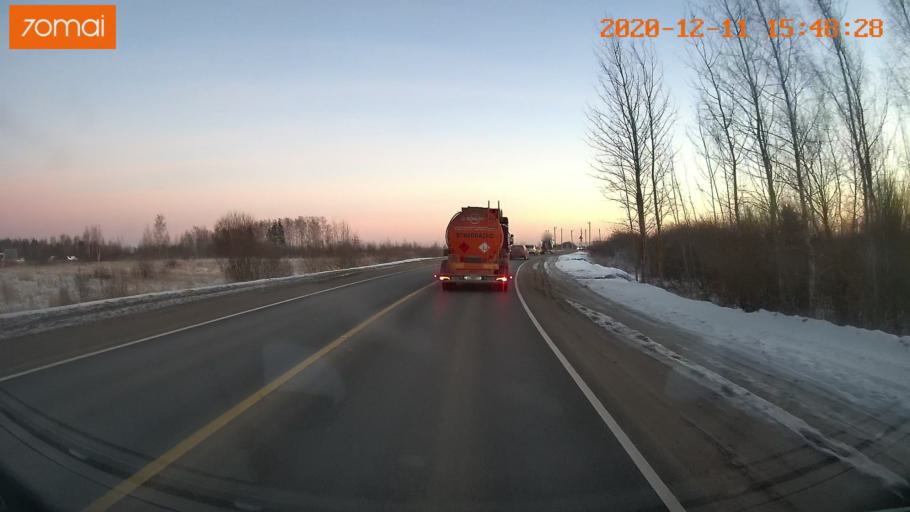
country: RU
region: Ivanovo
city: Novo-Talitsy
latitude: 56.9926
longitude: 40.8685
